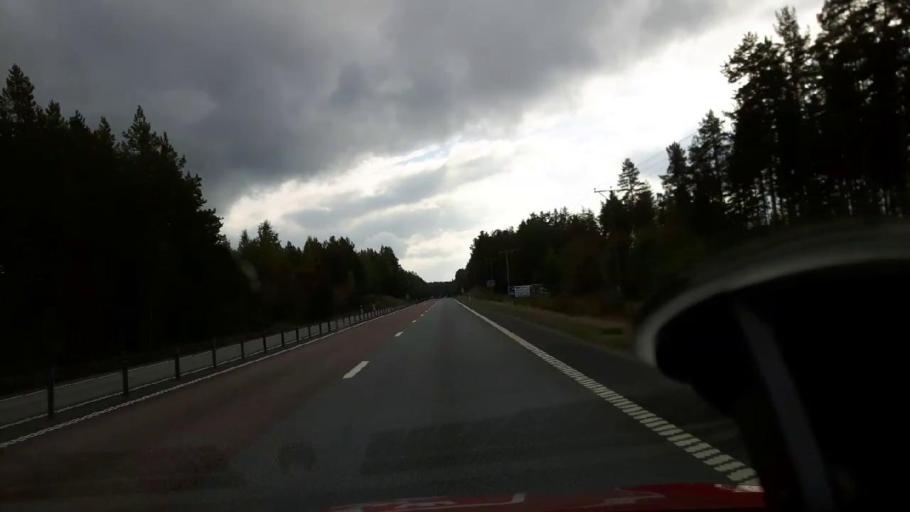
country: SE
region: Gaevleborg
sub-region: Gavle Kommun
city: Norrsundet
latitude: 61.0154
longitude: 16.9795
